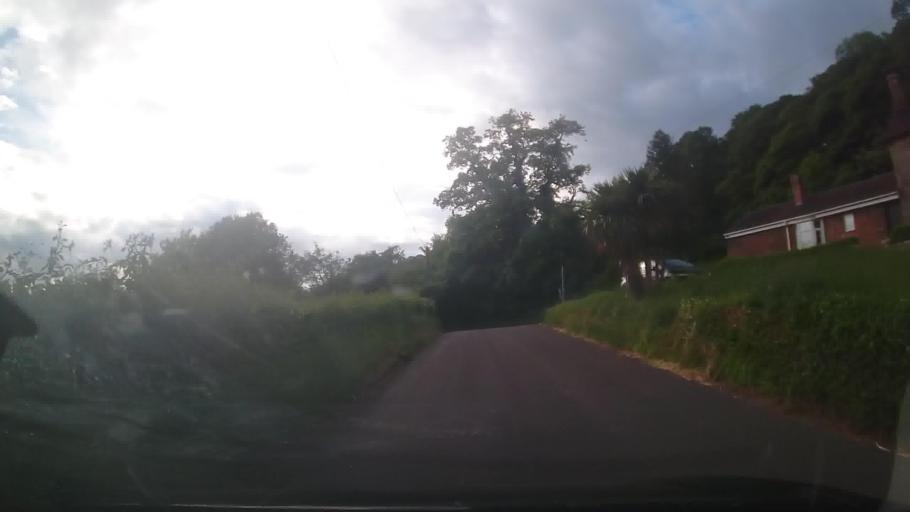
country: GB
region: England
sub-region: Shropshire
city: Prees
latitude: 52.8566
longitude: -2.6063
